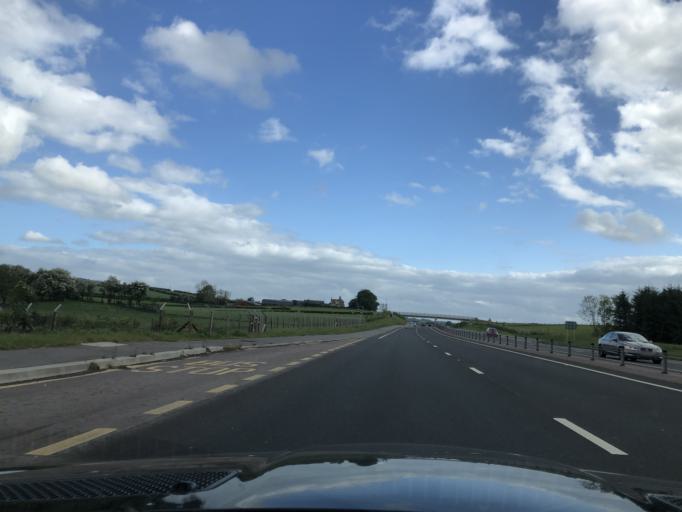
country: GB
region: Northern Ireland
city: Dunloy
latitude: 54.9703
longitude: -6.3429
